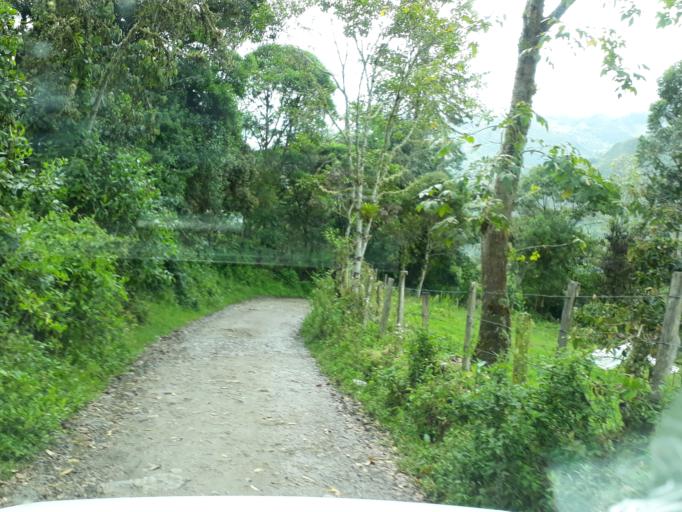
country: CO
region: Cundinamarca
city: Gacheta
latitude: 4.8563
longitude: -73.6433
